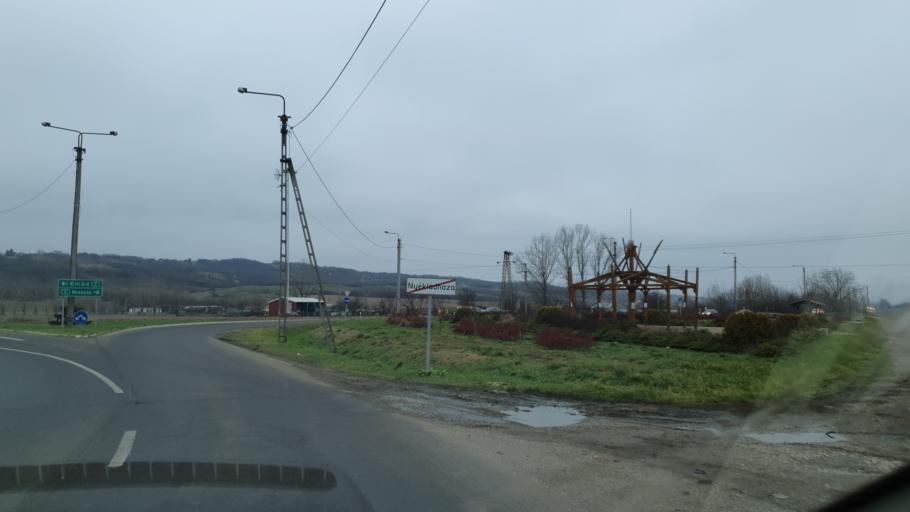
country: HU
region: Borsod-Abauj-Zemplen
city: Nyekladhaza
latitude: 47.9997
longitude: 20.8323
